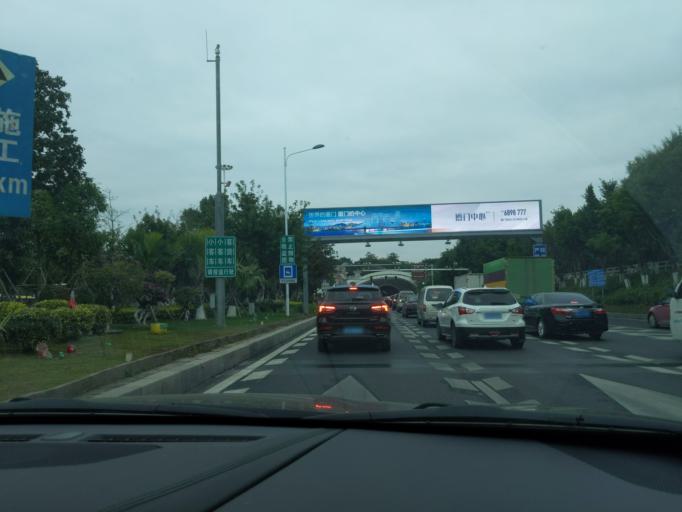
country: CN
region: Fujian
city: Liuwudian
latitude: 24.5159
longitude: 118.1798
